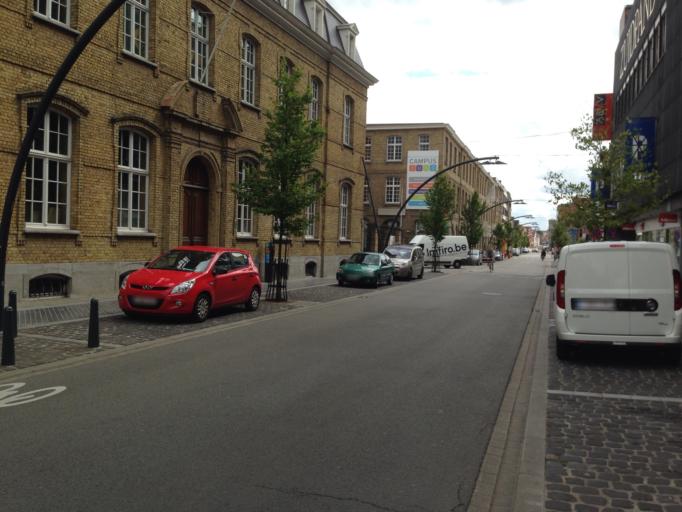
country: BE
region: Flanders
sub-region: Provincie West-Vlaanderen
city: Roeselare
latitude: 50.9436
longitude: 3.1243
